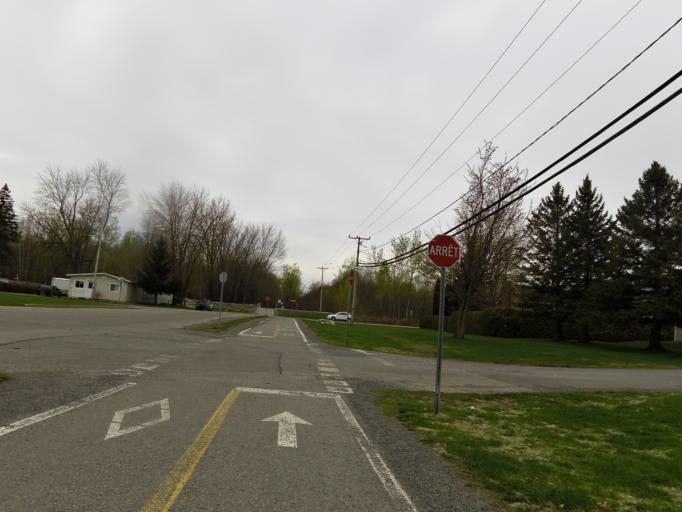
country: CA
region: Quebec
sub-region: Laurentides
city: Sainte-Marthe-sur-le-Lac
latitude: 45.5193
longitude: -73.9507
